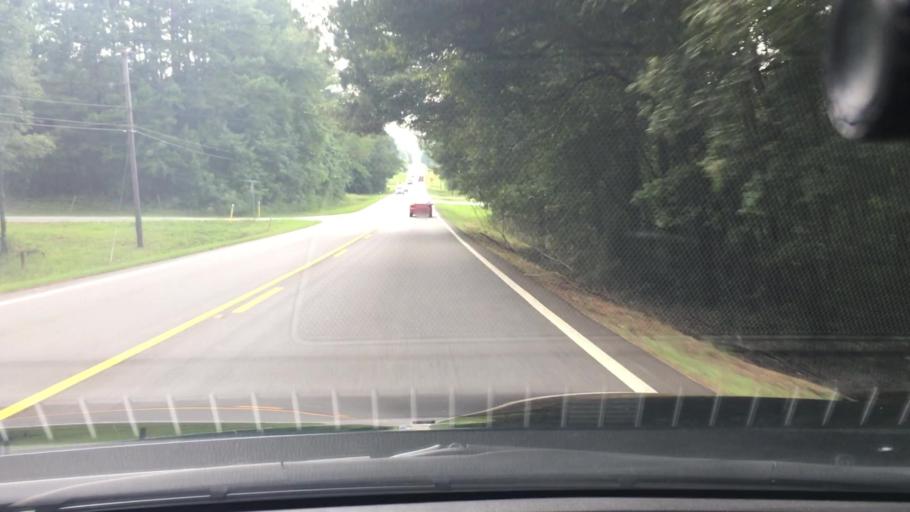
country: US
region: Georgia
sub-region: Coweta County
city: East Newnan
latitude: 33.3318
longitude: -84.7032
